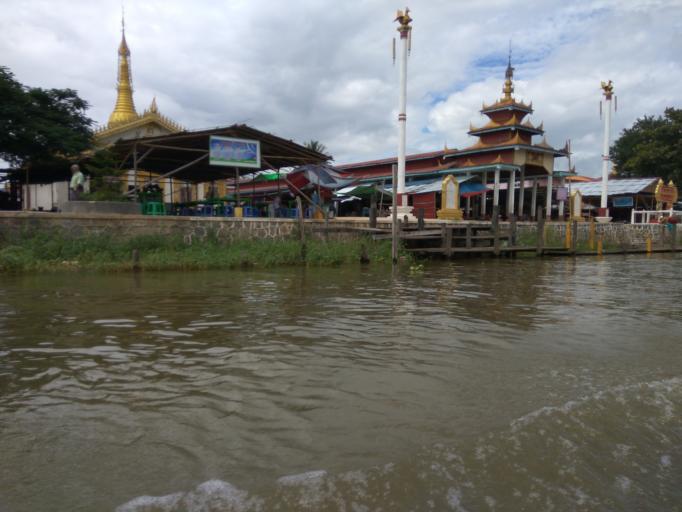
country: MM
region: Shan
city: Taunggyi
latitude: 20.4593
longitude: 96.9052
